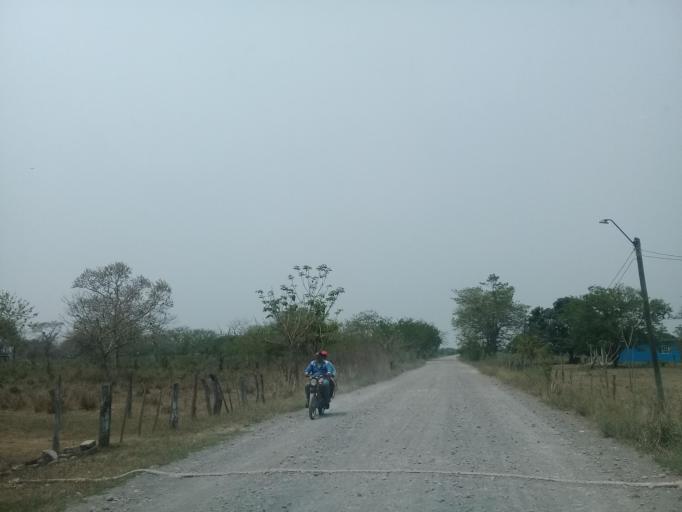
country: MX
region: Veracruz
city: Jamapa
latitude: 18.9346
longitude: -96.2169
